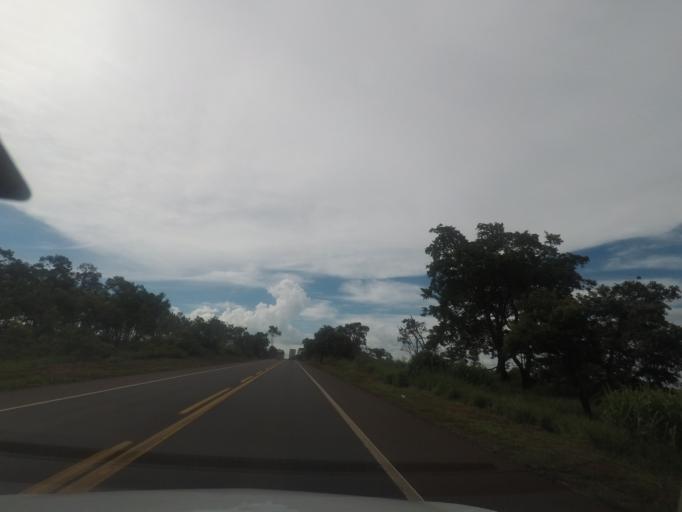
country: BR
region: Minas Gerais
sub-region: Prata
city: Prata
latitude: -19.2547
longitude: -48.9250
